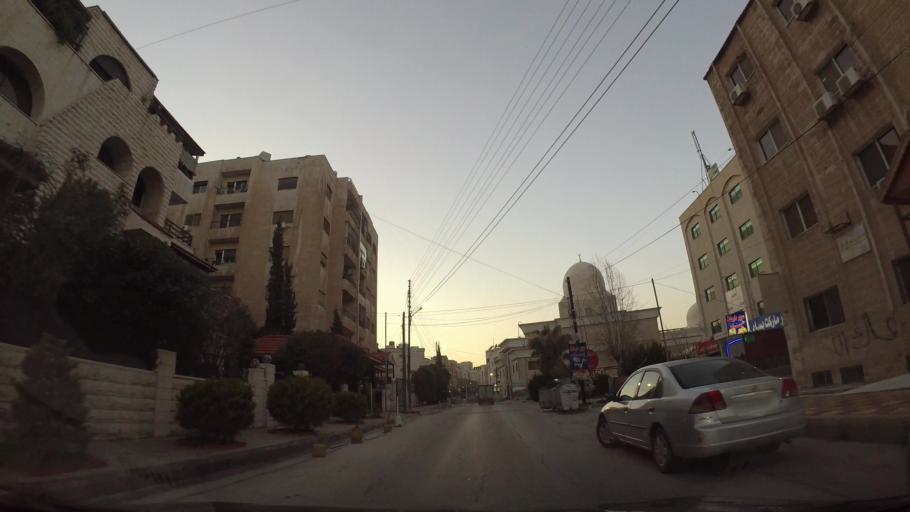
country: JO
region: Amman
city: Al Jubayhah
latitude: 31.9923
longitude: 35.8889
